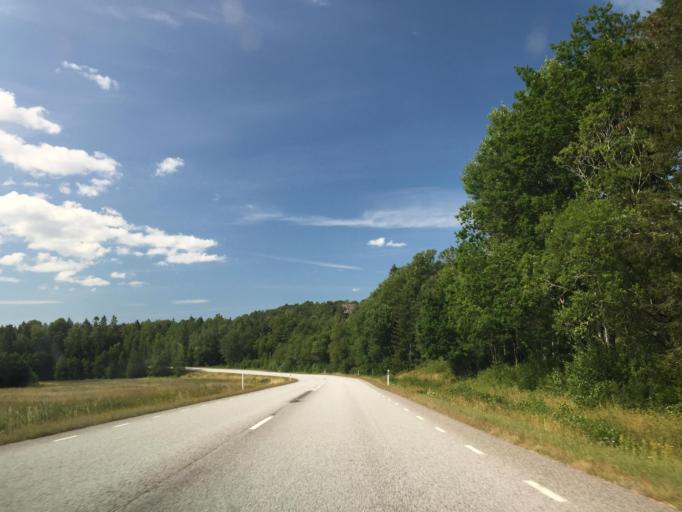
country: SE
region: Vaestra Goetaland
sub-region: Tanums Kommun
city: Tanumshede
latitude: 58.8205
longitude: 11.2596
